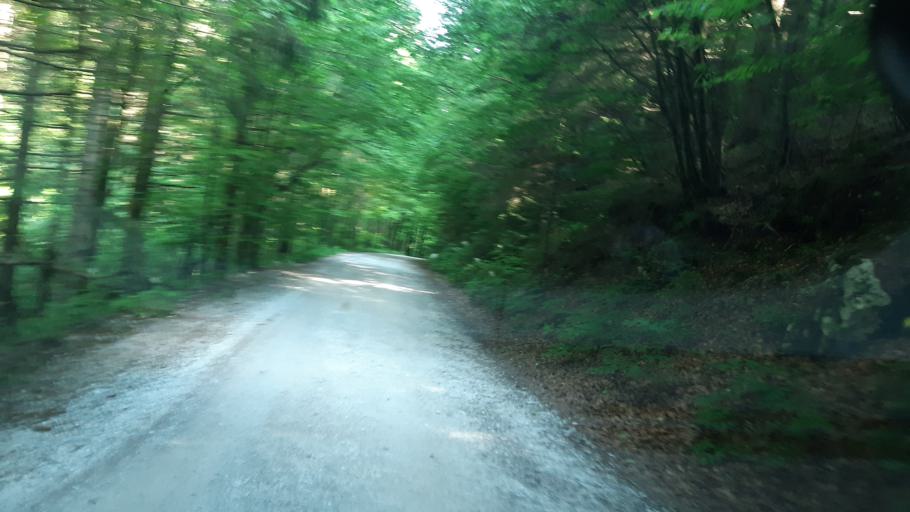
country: SI
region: Trzic
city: Bistrica pri Trzicu
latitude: 46.3697
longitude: 14.2764
